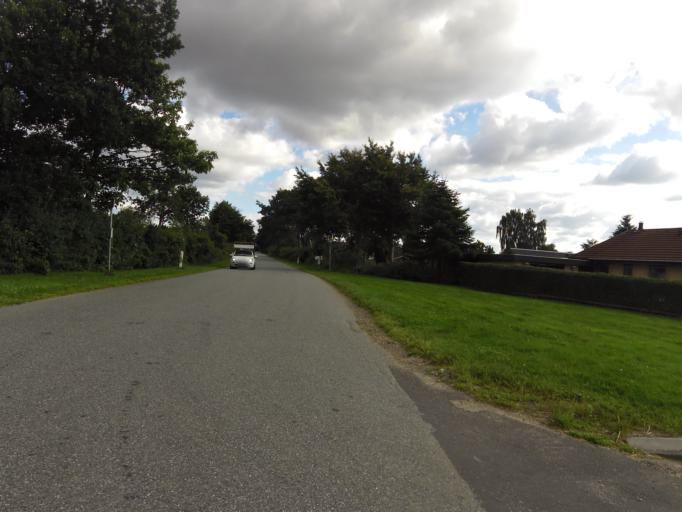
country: DK
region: South Denmark
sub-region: Haderslev Kommune
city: Haderslev
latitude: 55.2121
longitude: 9.4418
